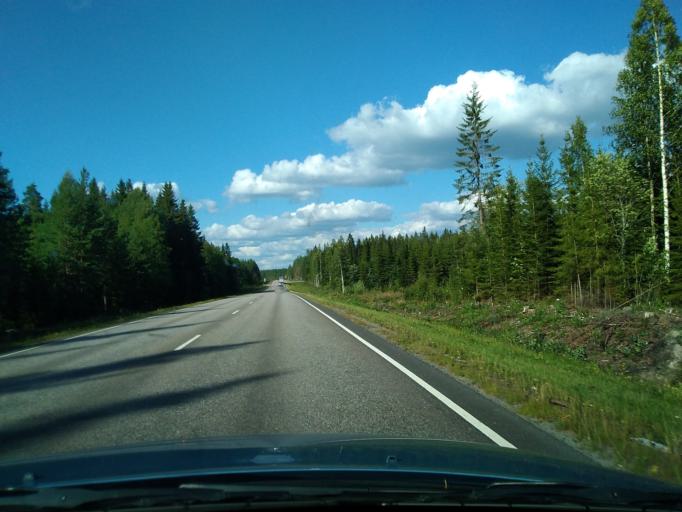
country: FI
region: Pirkanmaa
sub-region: Ylae-Pirkanmaa
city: Maenttae
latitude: 62.0426
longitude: 24.7125
